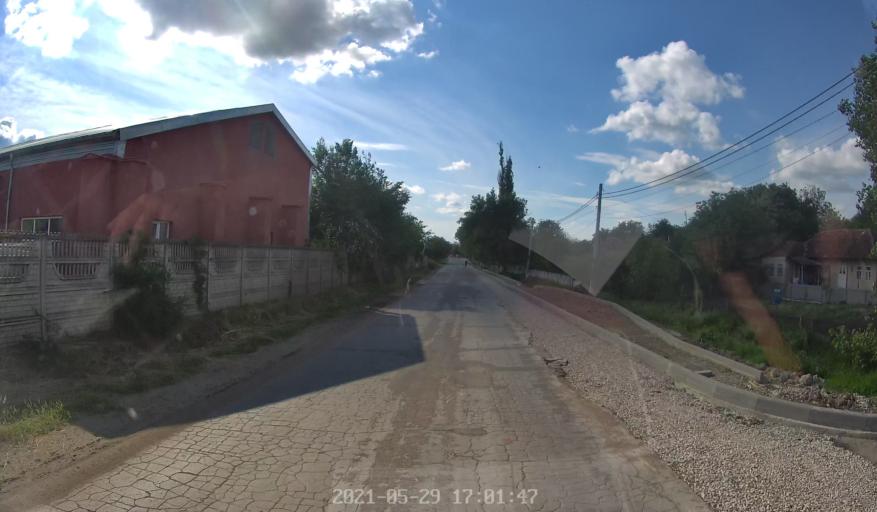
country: MD
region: Laloveni
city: Ialoveni
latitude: 46.8331
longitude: 28.8561
